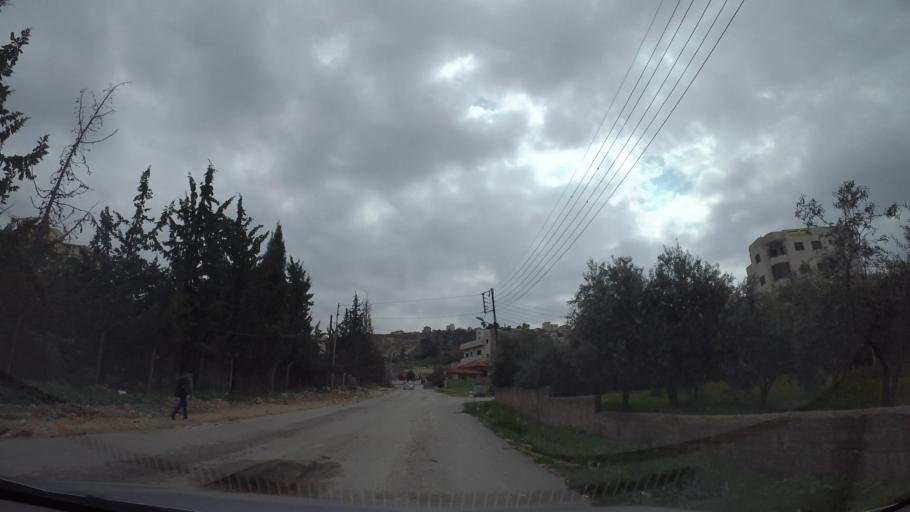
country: JO
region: Amman
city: Al Jubayhah
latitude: 32.0509
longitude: 35.8416
